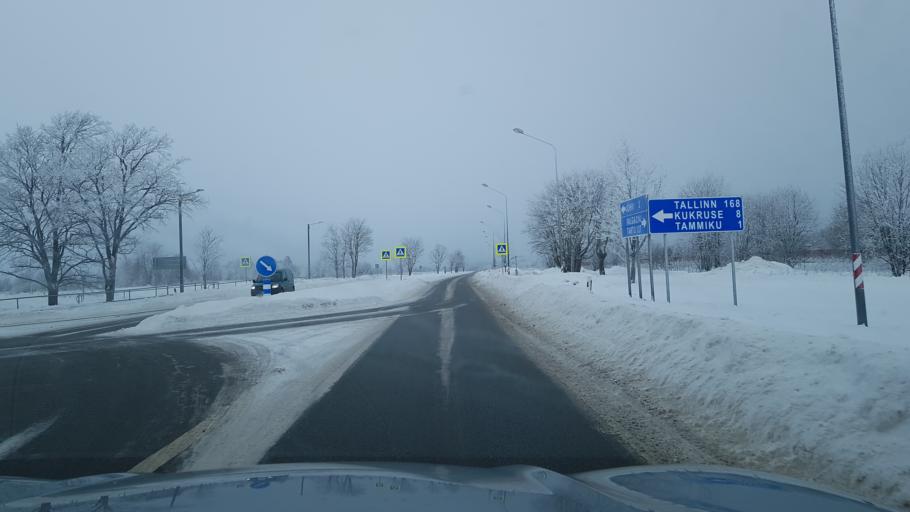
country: EE
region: Ida-Virumaa
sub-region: Johvi vald
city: Johvi
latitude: 59.3378
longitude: 27.4029
